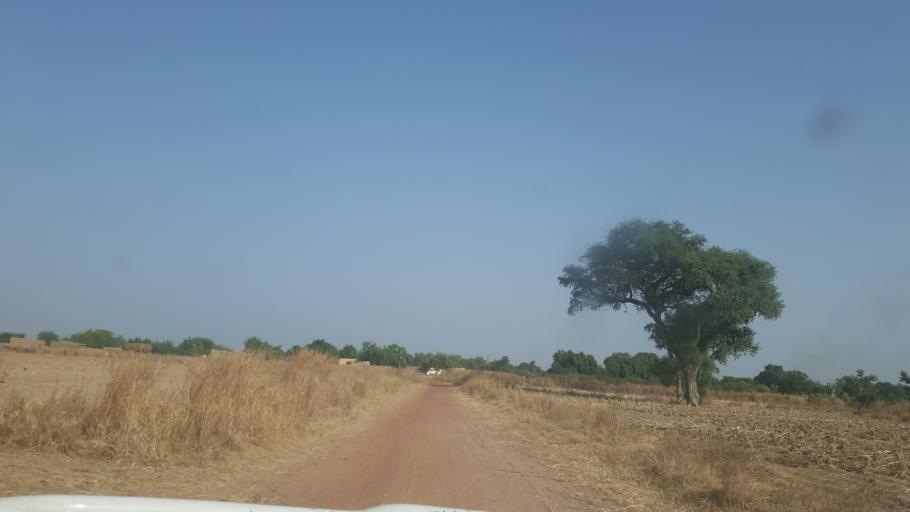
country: ML
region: Segou
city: Baroueli
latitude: 13.3534
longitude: -6.9354
